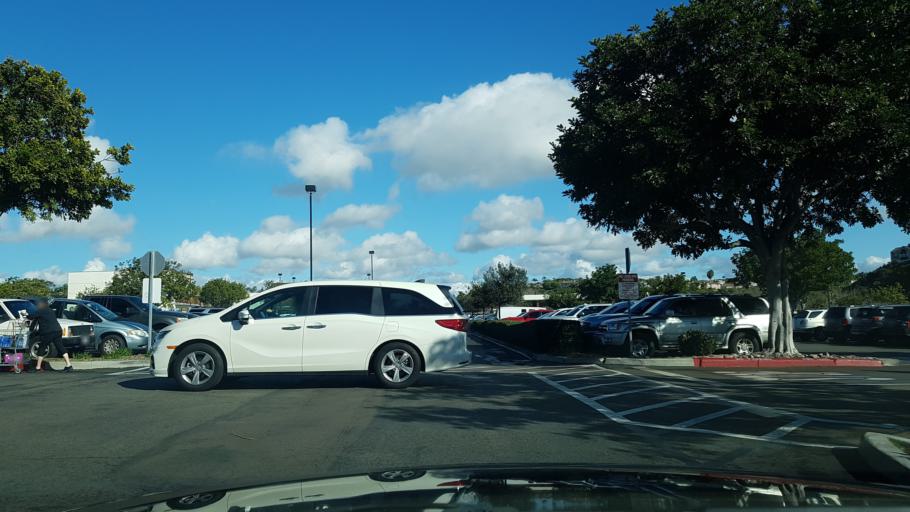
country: US
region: California
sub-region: San Diego County
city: Carlsbad
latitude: 33.1211
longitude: -117.3160
